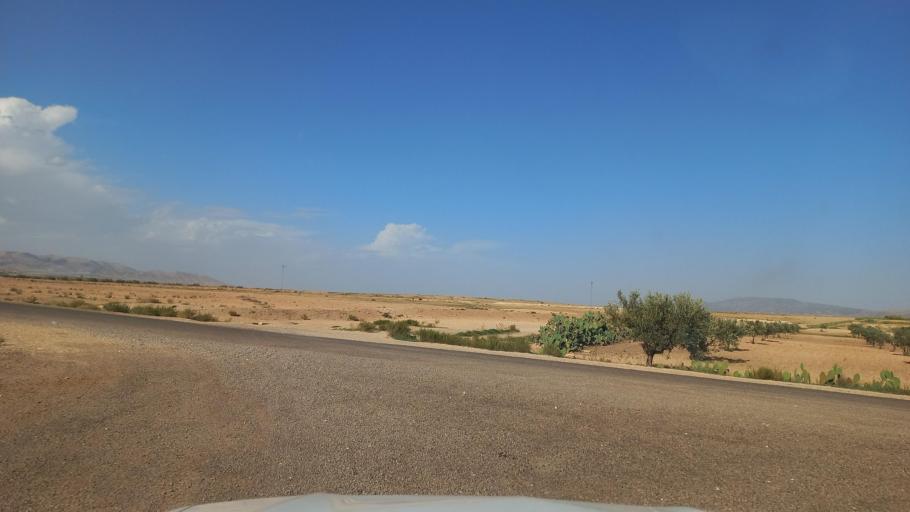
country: TN
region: Al Qasrayn
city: Sbiba
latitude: 35.3205
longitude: 9.0164
